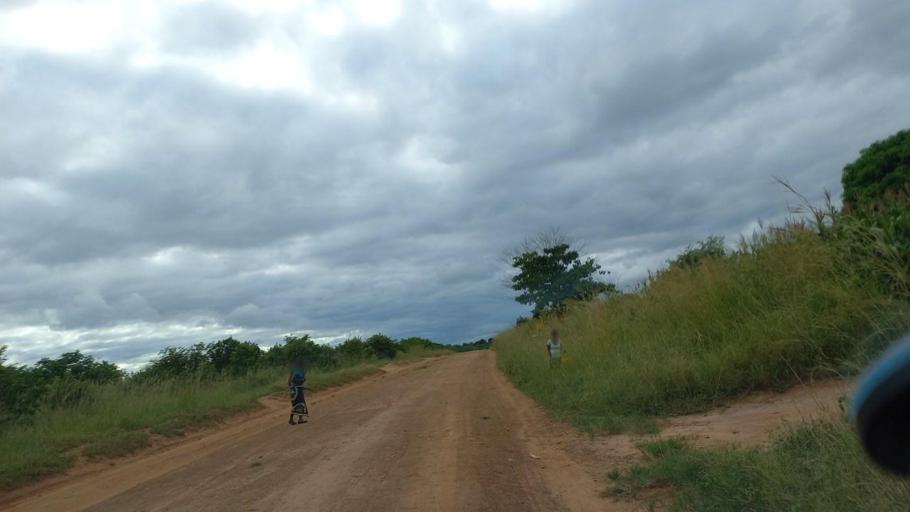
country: ZM
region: Lusaka
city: Chongwe
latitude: -15.4506
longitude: 28.8462
